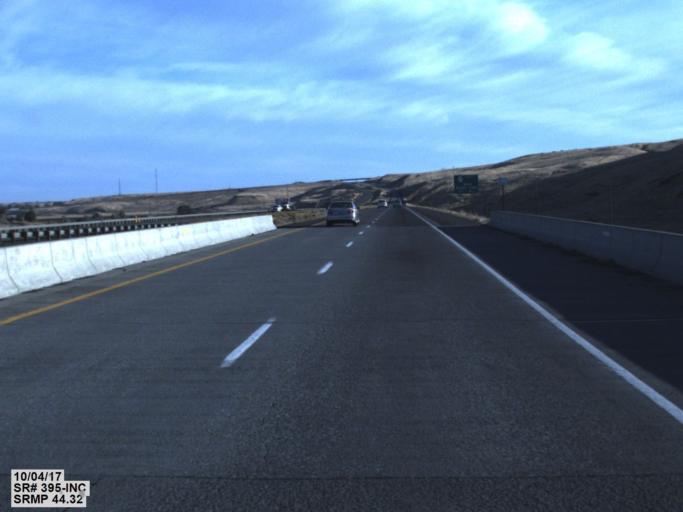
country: US
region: Washington
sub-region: Franklin County
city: Basin City
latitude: 46.5465
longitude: -119.0062
